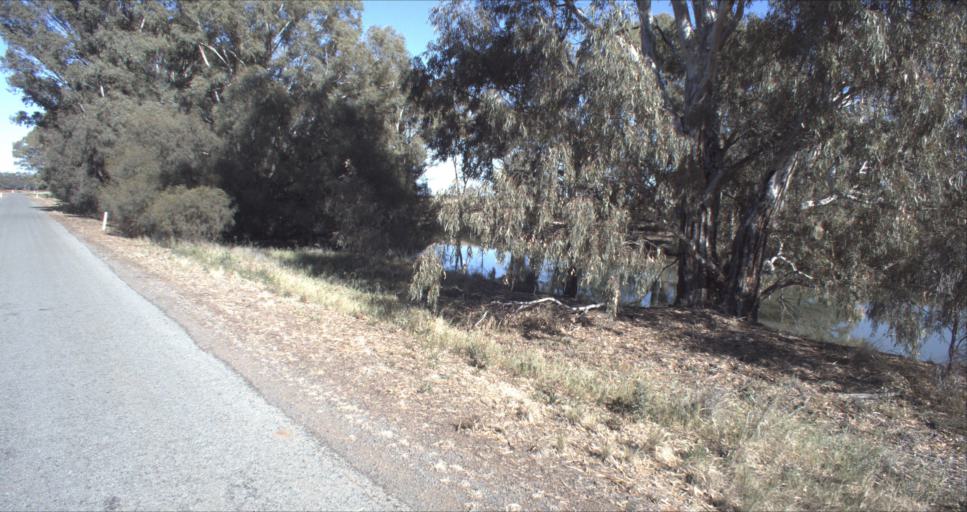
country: AU
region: New South Wales
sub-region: Leeton
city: Leeton
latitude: -34.6057
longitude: 146.2594
